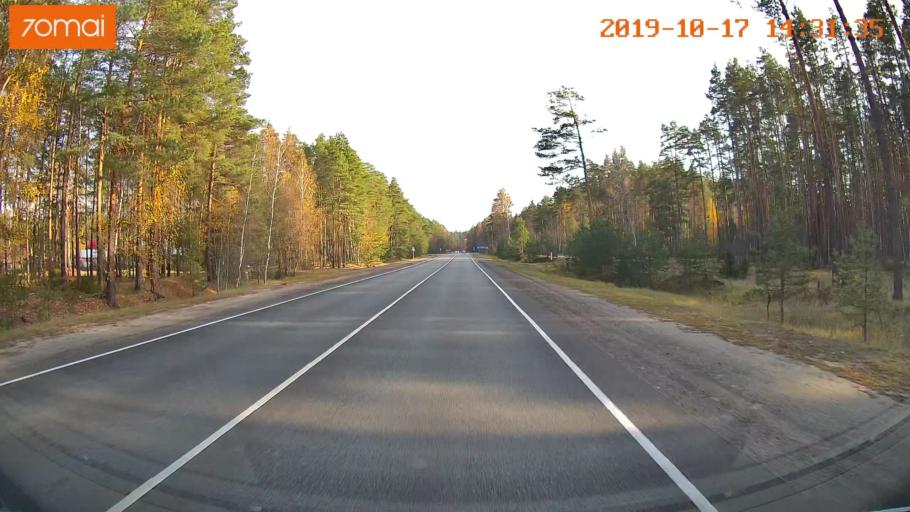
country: RU
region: Rjazan
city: Solotcha
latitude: 54.9352
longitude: 39.9661
